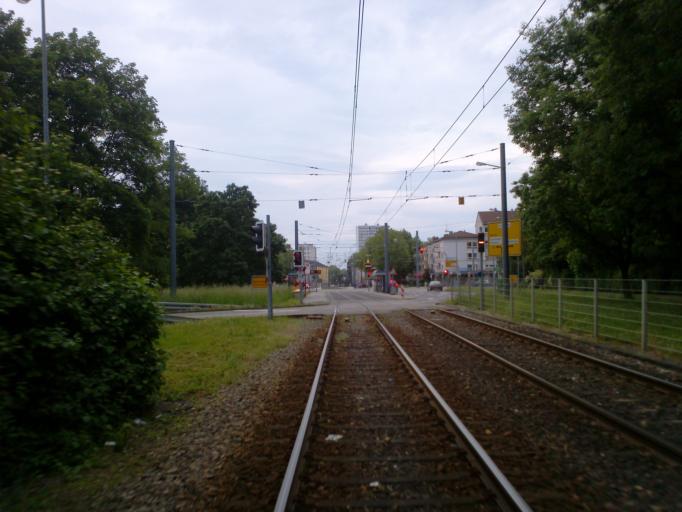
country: DE
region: Baden-Wuerttemberg
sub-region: Karlsruhe Region
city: Karlsruhe
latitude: 49.0095
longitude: 8.3599
